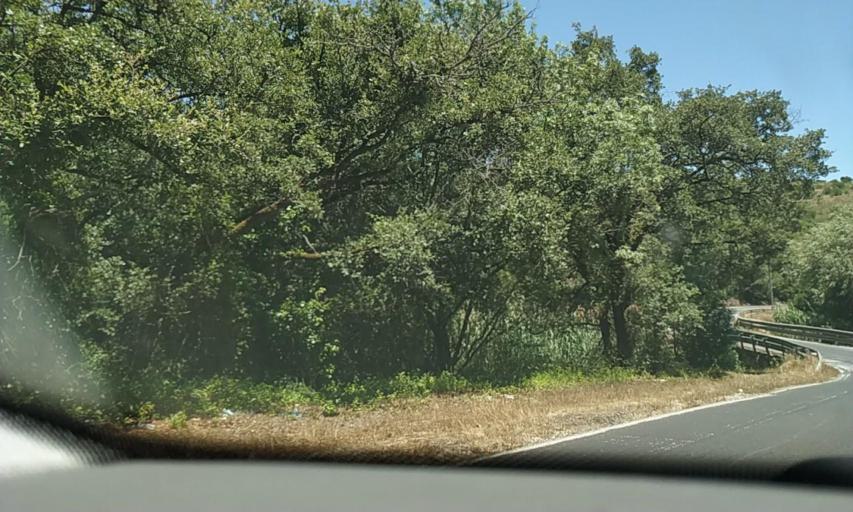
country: PT
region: Lisbon
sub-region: Sintra
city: Almargem
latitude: 38.8698
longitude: -9.2296
